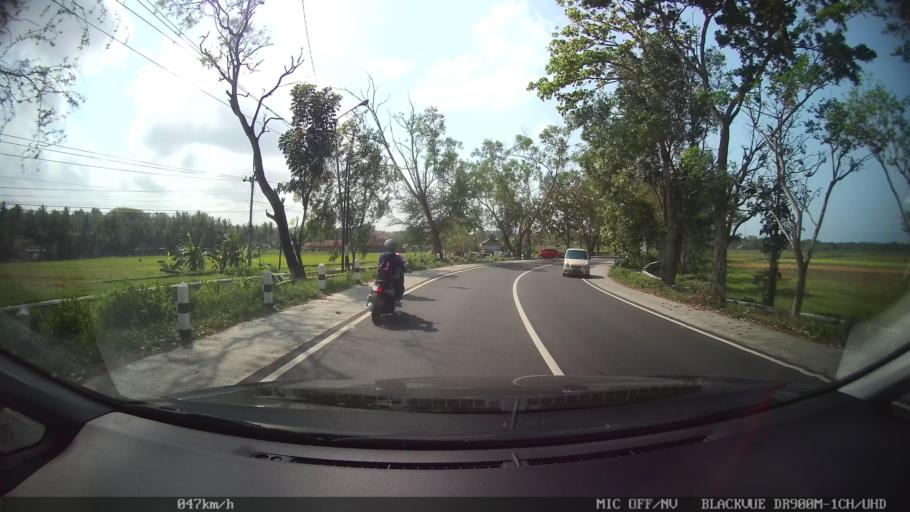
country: ID
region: Daerah Istimewa Yogyakarta
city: Srandakan
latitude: -7.8975
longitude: 110.1627
